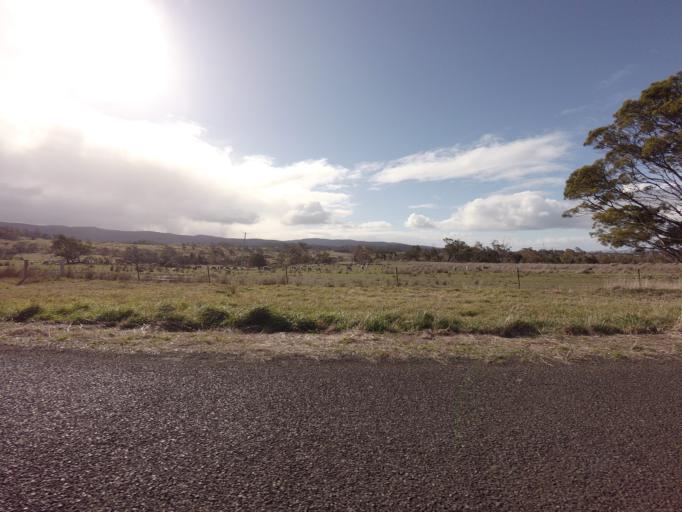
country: AU
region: Tasmania
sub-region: Sorell
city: Sorell
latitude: -42.3001
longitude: 147.9878
